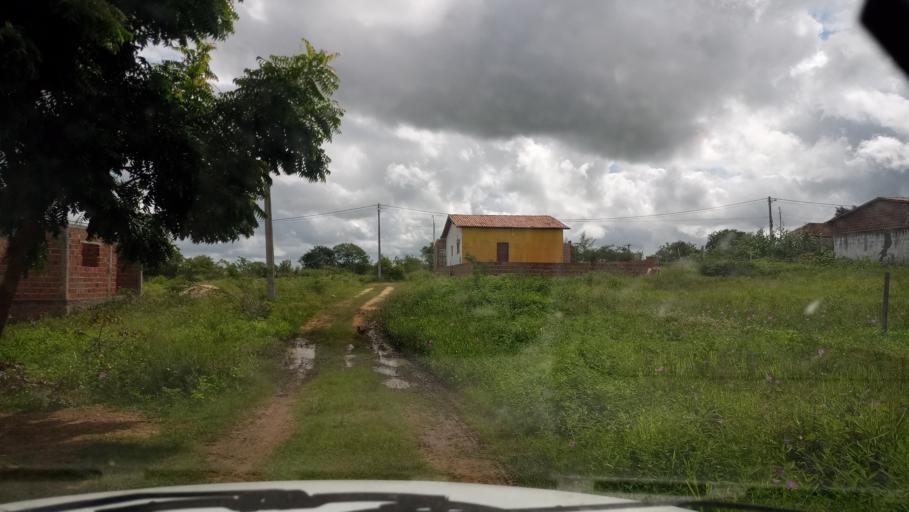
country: BR
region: Rio Grande do Norte
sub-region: Brejinho
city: Brejinho
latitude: -6.1466
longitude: -35.4310
